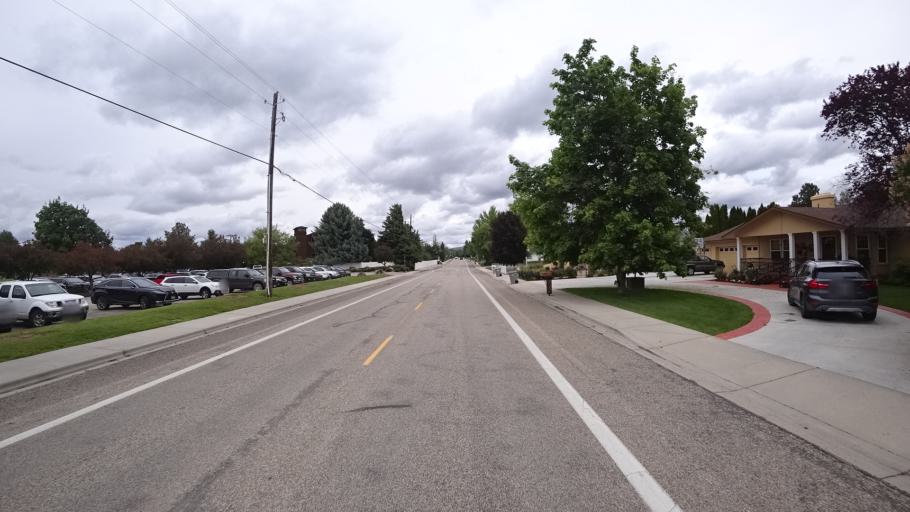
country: US
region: Idaho
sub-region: Ada County
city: Eagle
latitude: 43.7012
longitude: -116.3341
